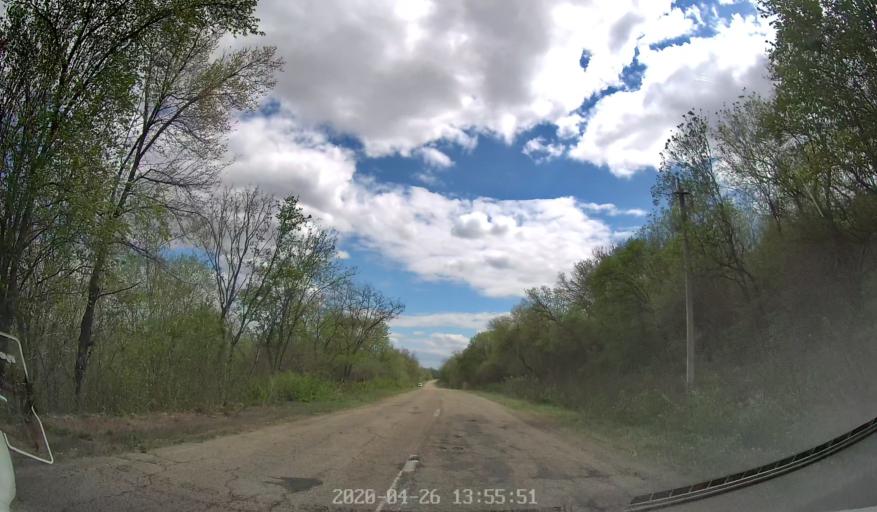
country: MD
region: Telenesti
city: Cocieri
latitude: 47.2833
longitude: 29.1036
